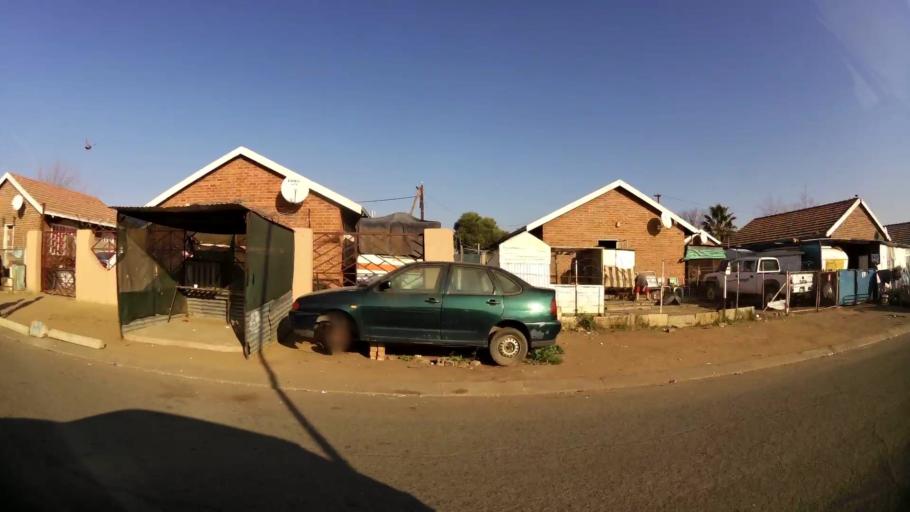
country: ZA
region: Orange Free State
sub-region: Mangaung Metropolitan Municipality
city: Bloemfontein
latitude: -29.1555
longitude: 26.2158
